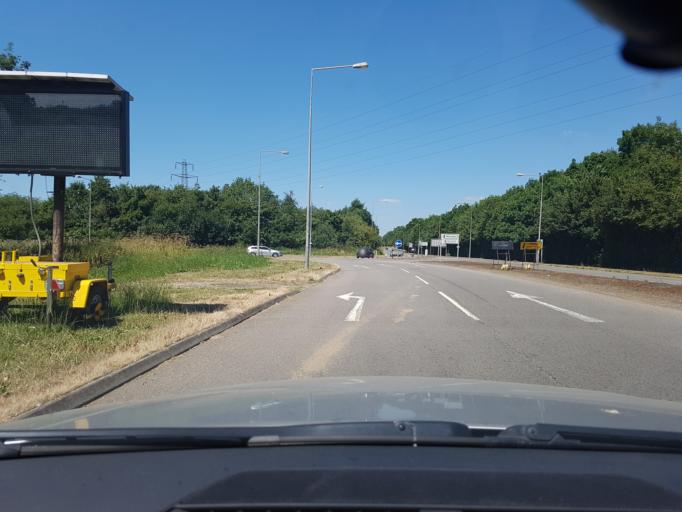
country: GB
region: England
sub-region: Milton Keynes
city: Calverton
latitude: 52.0405
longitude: -0.8192
